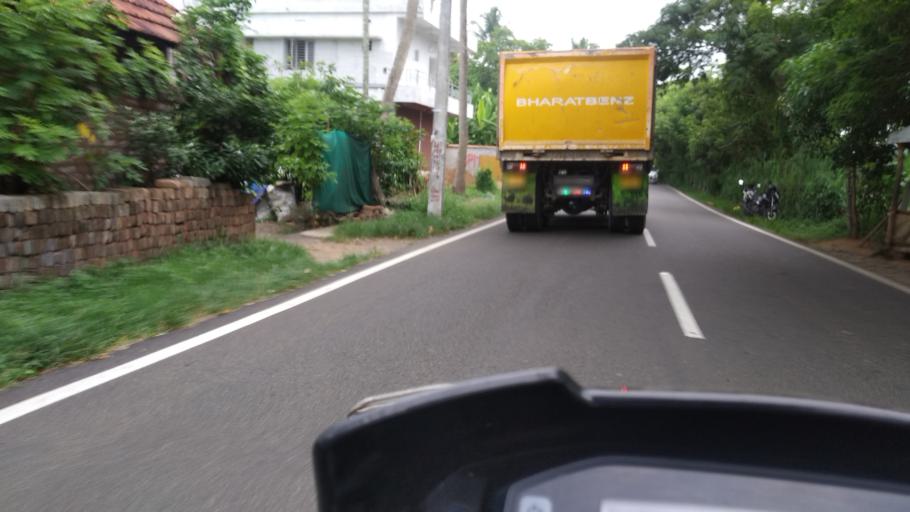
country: IN
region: Kerala
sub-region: Ernakulam
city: Aluva
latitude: 10.1551
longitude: 76.2812
